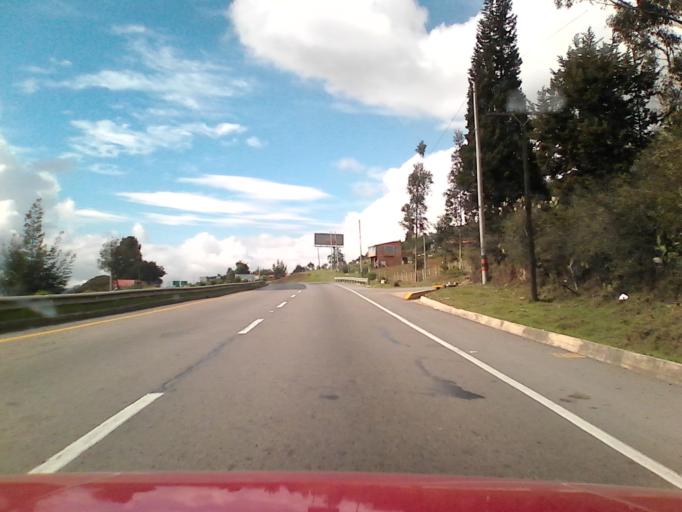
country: CO
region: Boyaca
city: Combita
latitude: 5.6105
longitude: -73.3249
